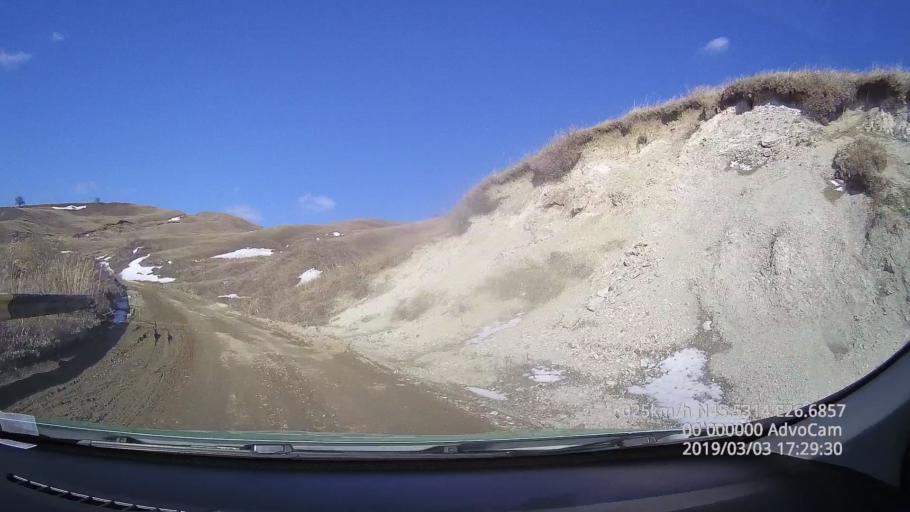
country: RO
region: Buzau
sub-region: Comuna Bisoca
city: Bisoca
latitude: 45.5315
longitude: 26.6858
